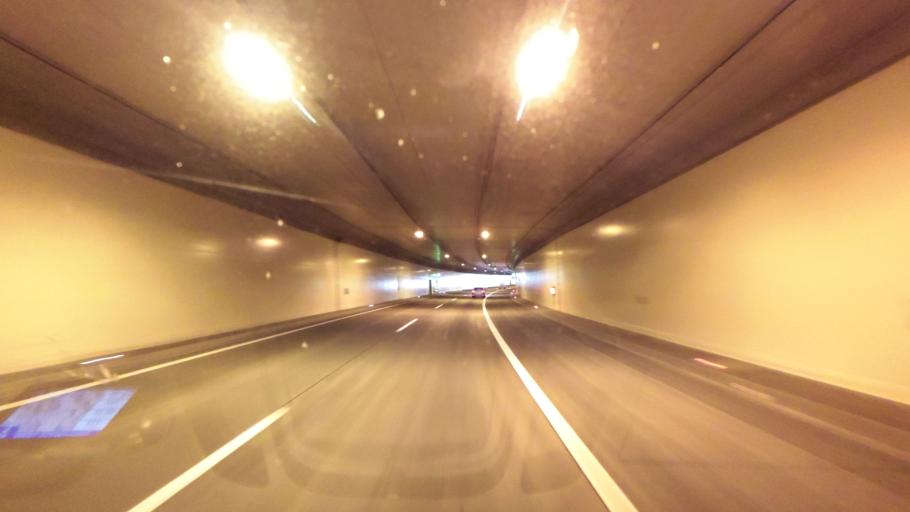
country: AT
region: Carinthia
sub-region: Politischer Bezirk Spittal an der Drau
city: Trebesing
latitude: 46.8815
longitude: 13.5115
